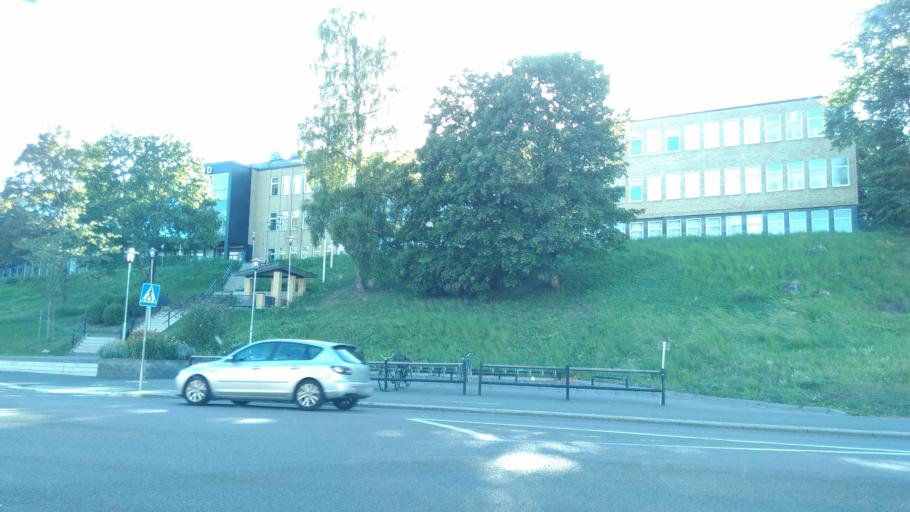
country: SE
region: Vaestra Goetaland
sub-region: Skovde Kommun
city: Skoevde
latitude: 58.3893
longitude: 13.8418
